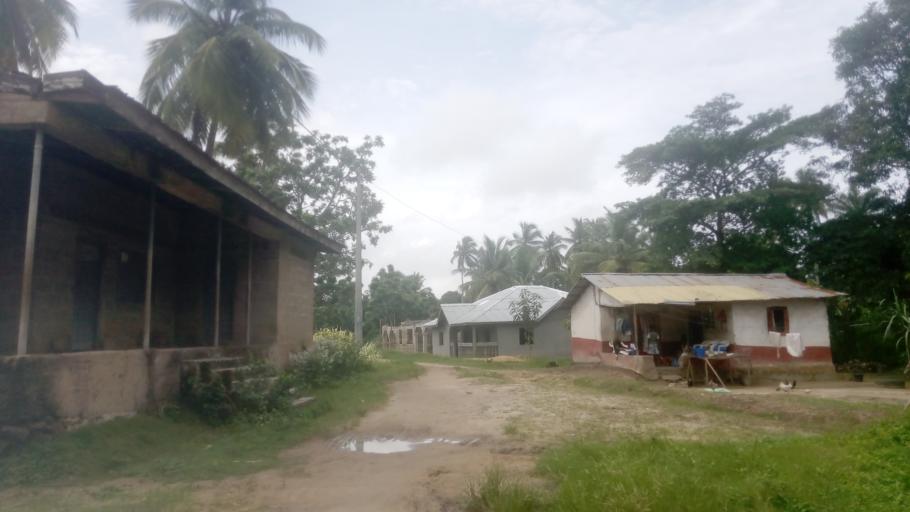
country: SL
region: Northern Province
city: Lunsar
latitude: 8.6878
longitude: -12.5377
